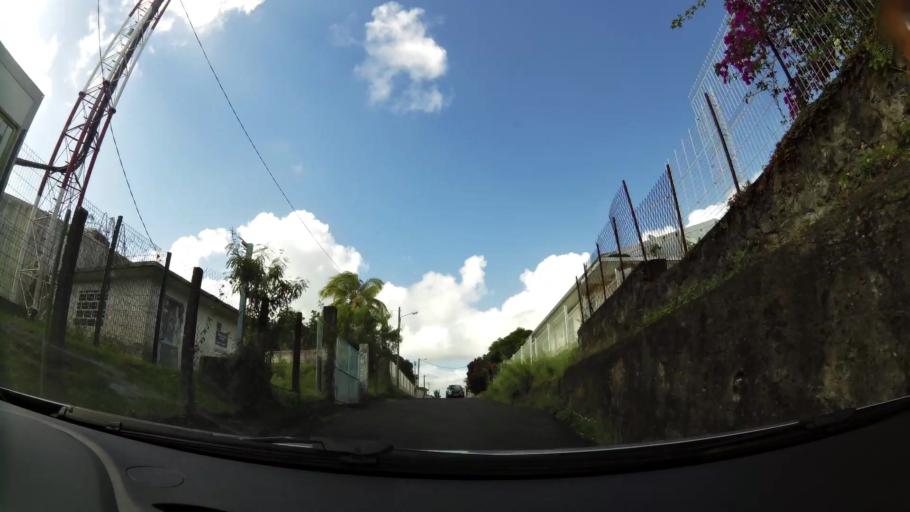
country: MQ
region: Martinique
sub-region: Martinique
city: Fort-de-France
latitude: 14.6259
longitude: -61.0583
